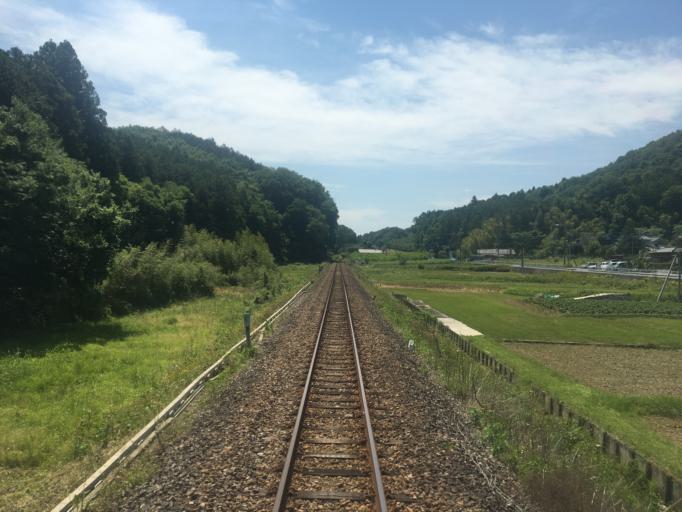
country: JP
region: Saitama
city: Ogawa
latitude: 36.0380
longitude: 139.2632
